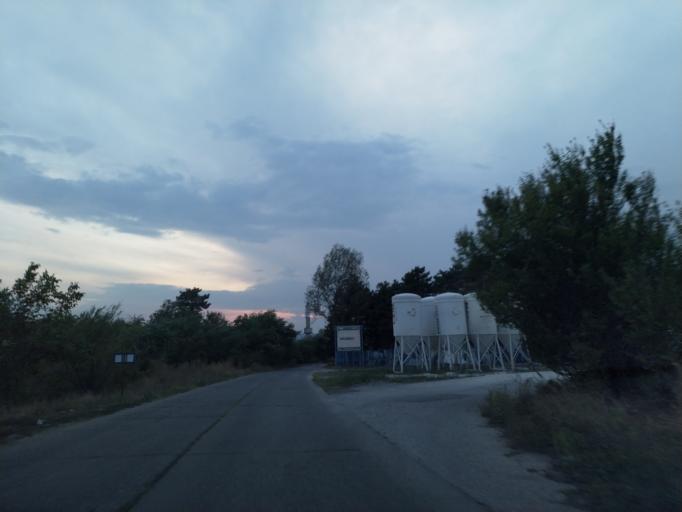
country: RS
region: Central Serbia
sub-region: Pomoravski Okrug
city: Paracin
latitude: 43.8654
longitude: 21.4384
